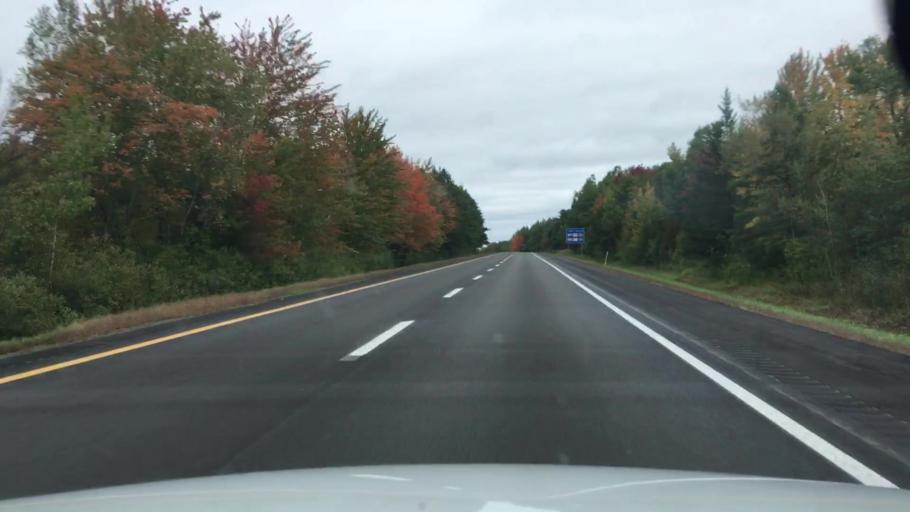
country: US
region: Maine
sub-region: Penobscot County
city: Orono
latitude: 44.8901
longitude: -68.6931
